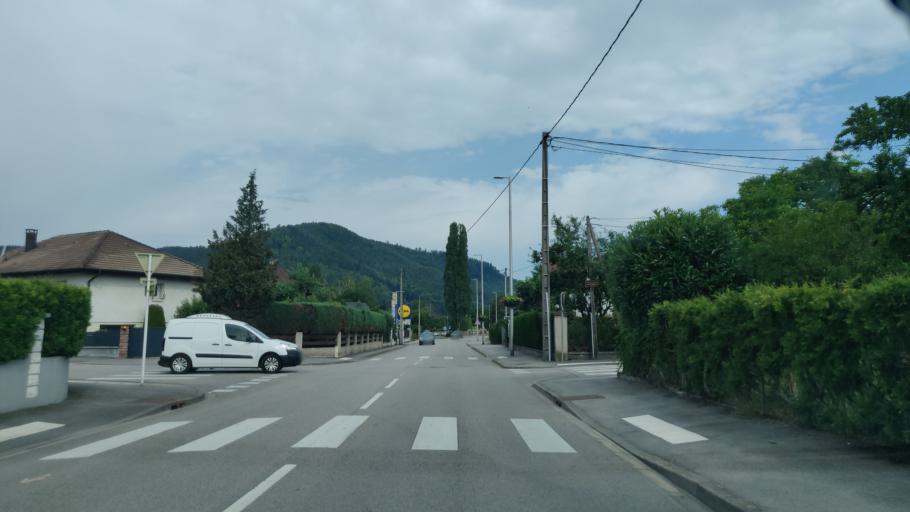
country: FR
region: Lorraine
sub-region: Departement des Vosges
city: Saint-Die-des-Vosges
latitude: 48.2906
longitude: 6.9346
